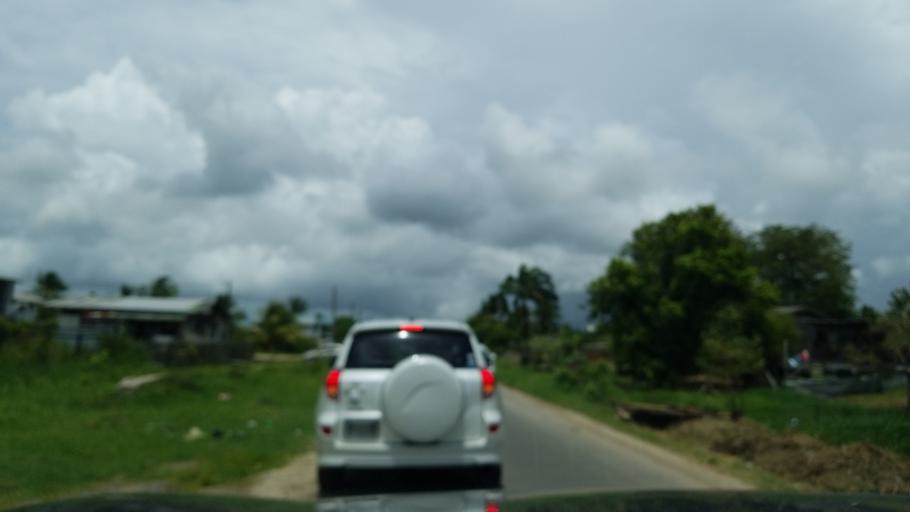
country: GY
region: Demerara-Mahaica
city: Georgetown
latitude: 6.8009
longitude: -58.1235
